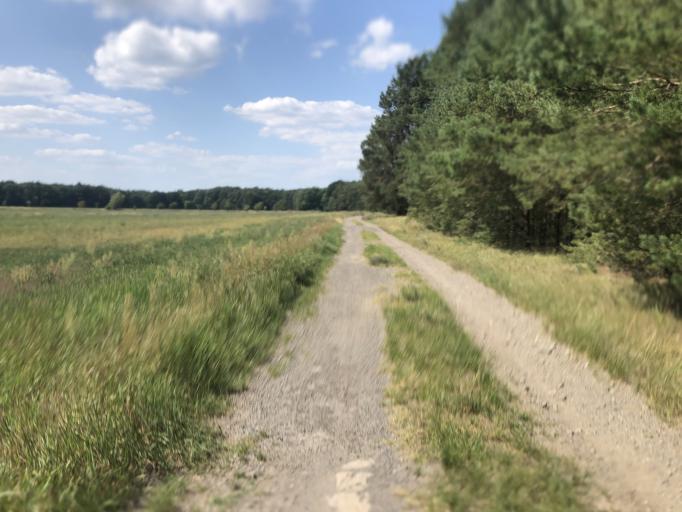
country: DE
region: Brandenburg
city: Mullrose
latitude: 52.2322
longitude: 14.4023
